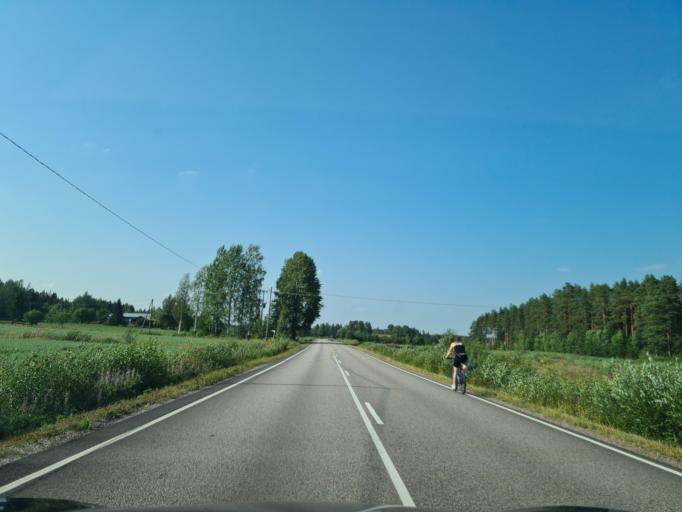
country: FI
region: Satakunta
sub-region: Pohjois-Satakunta
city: Karvia
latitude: 62.2129
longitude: 22.6073
